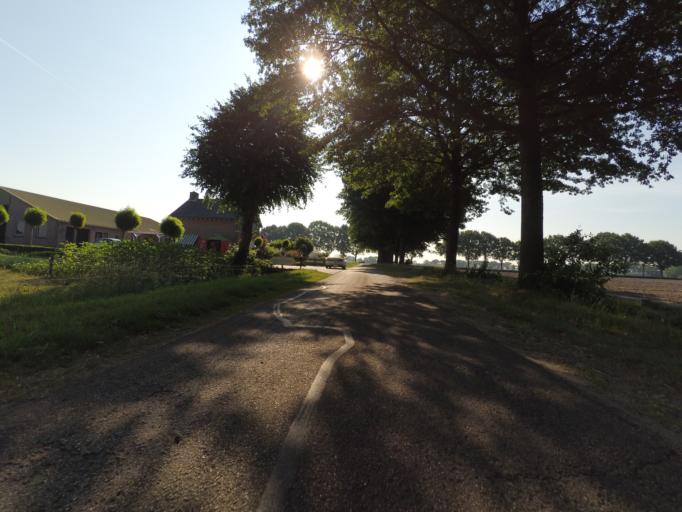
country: NL
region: North Brabant
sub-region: Gemeente Woensdrecht
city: Woensdrecht
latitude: 51.4384
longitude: 4.3867
